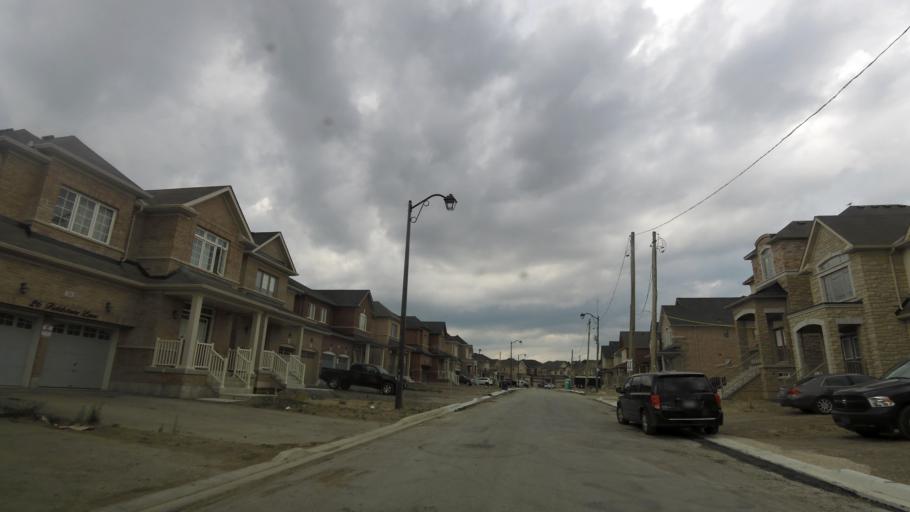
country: CA
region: Ontario
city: Brampton
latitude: 43.7523
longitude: -79.8391
